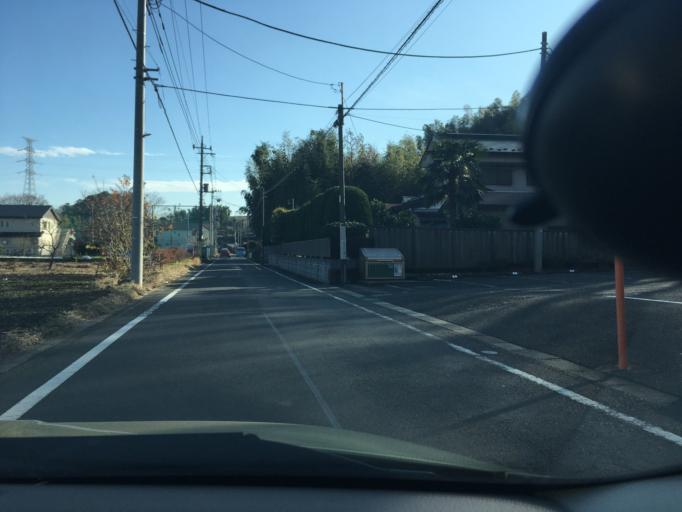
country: JP
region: Tokyo
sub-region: Machida-shi
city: Machida
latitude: 35.5637
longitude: 139.4141
